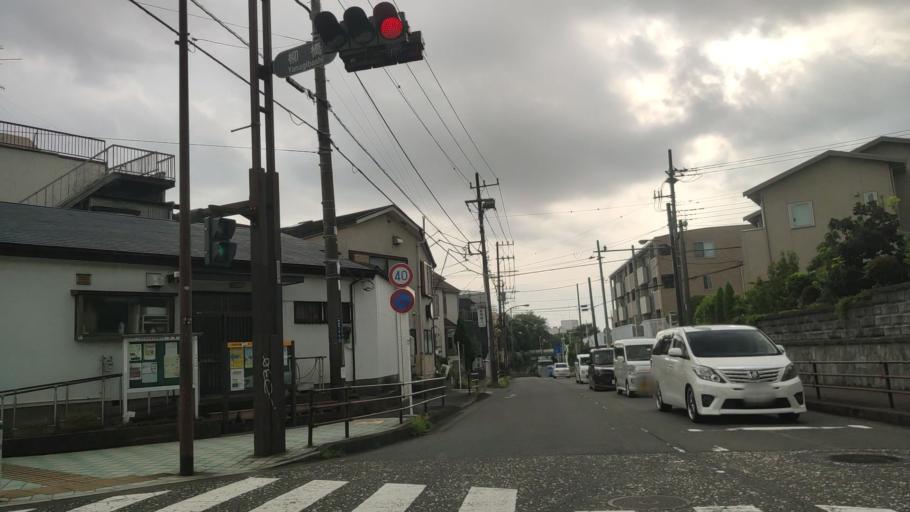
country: JP
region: Kanagawa
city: Minami-rinkan
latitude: 35.4609
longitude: 139.4611
